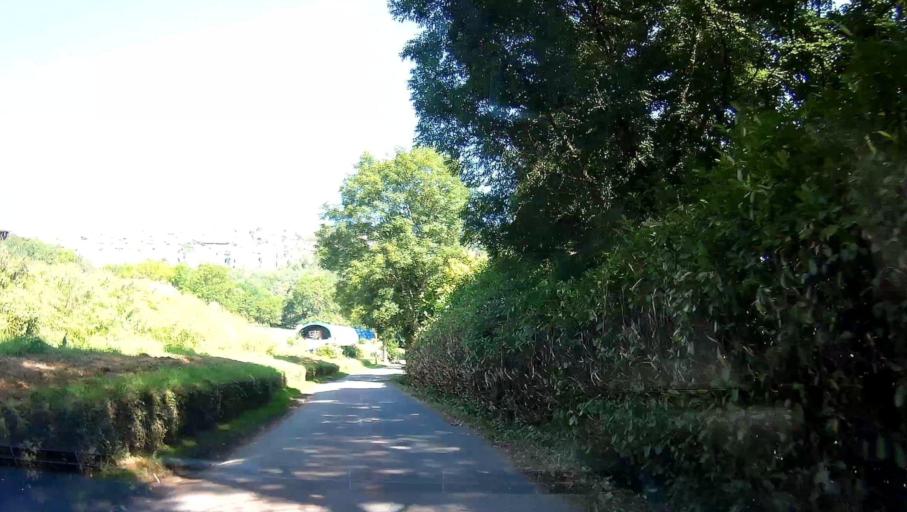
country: FR
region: Bourgogne
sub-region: Departement de la Cote-d'Or
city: Nolay
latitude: 46.9714
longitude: 4.6428
